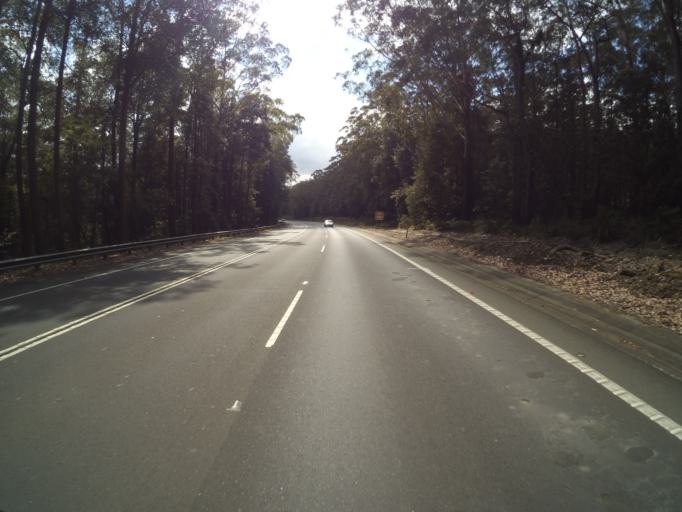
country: AU
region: New South Wales
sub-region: Wollongong
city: Mount Ousley
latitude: -34.3701
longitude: 150.8479
